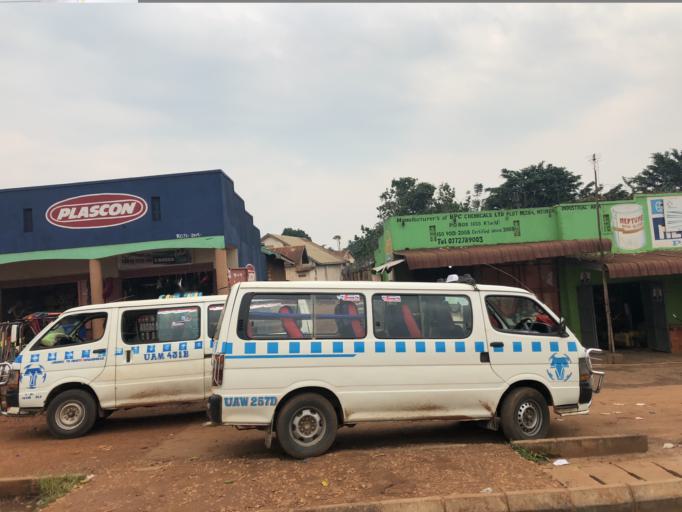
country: UG
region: Central Region
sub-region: Mukono District
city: Mukono
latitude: 0.3498
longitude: 32.7619
